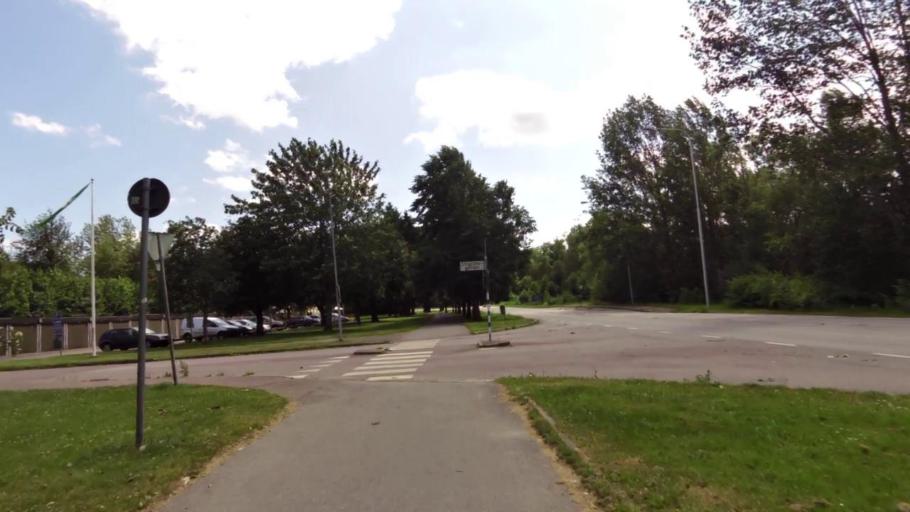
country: SE
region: OEstergoetland
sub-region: Linkopings Kommun
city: Malmslatt
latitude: 58.4264
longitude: 15.5689
